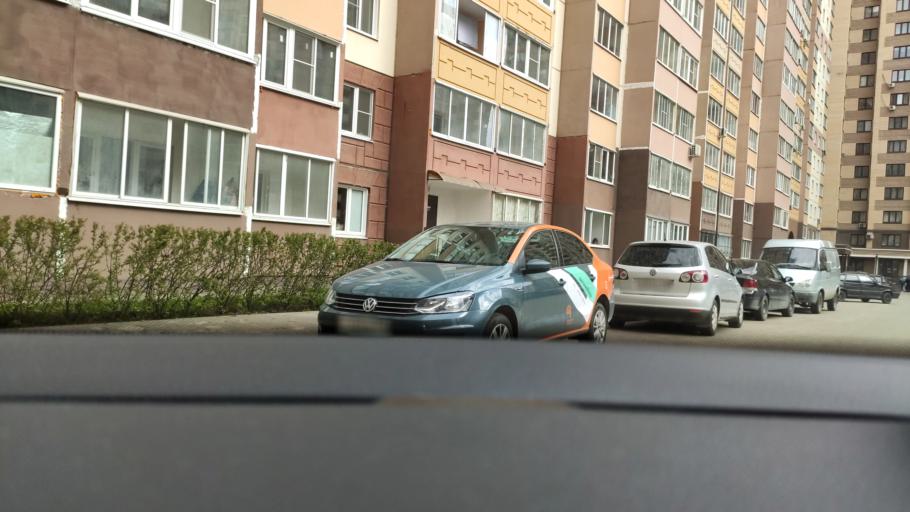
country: RU
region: Moskovskaya
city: Lesnoy Gorodok
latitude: 55.6567
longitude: 37.2265
